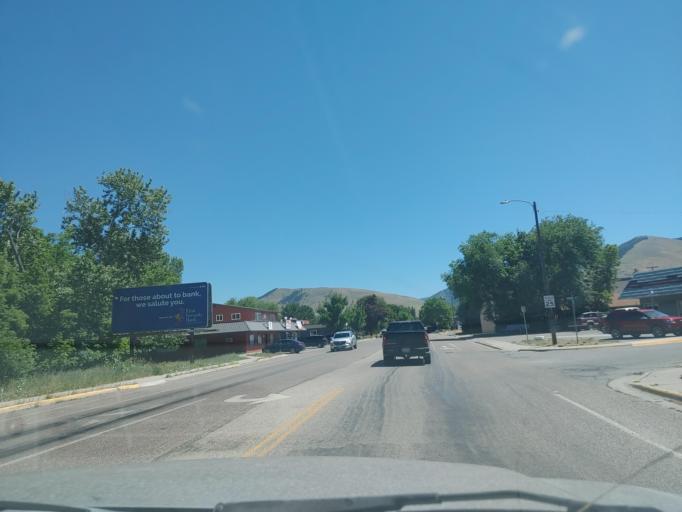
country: US
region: Montana
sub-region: Missoula County
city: Missoula
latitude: 46.8670
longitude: -114.0176
